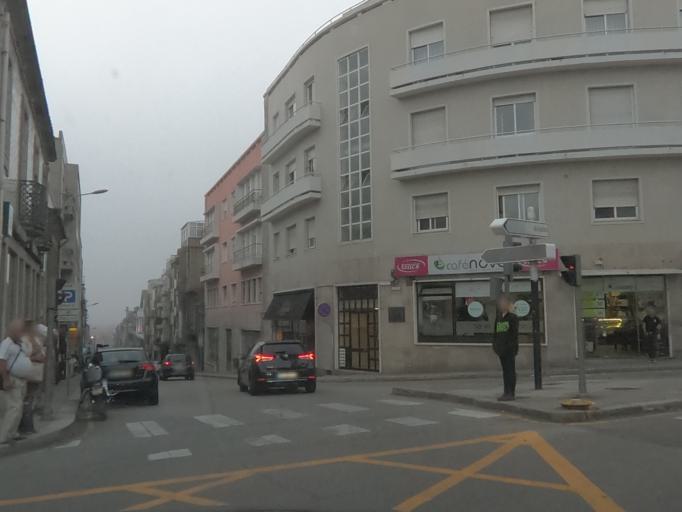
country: PT
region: Porto
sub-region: Porto
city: Porto
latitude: 41.1538
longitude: -8.6161
